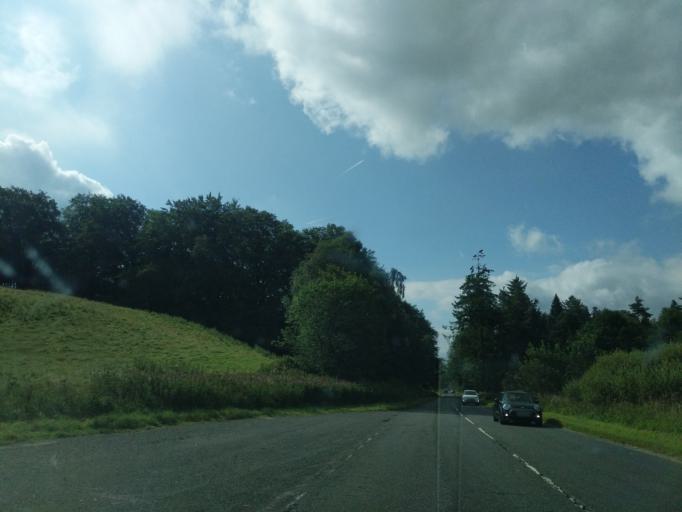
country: GB
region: Scotland
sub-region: Midlothian
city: Penicuik
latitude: 55.7458
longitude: -3.2044
